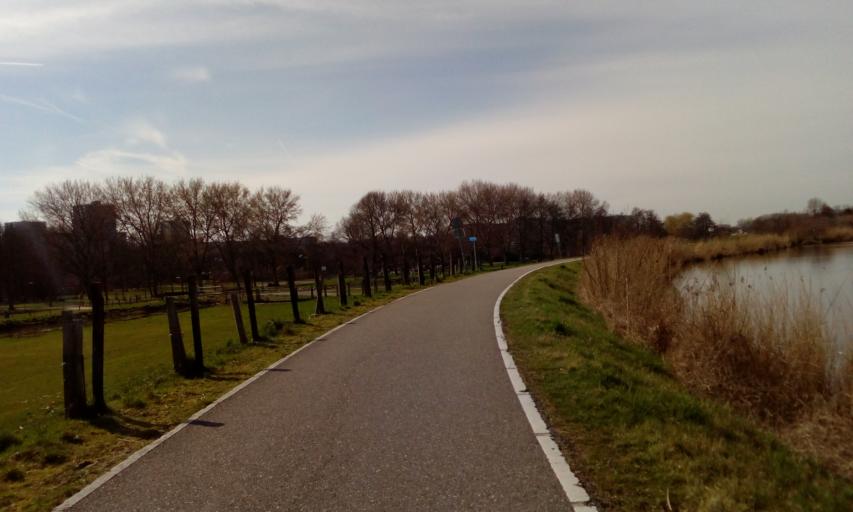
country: NL
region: South Holland
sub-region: Gemeente Lansingerland
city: Bleiswijk
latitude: 51.9683
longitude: 4.5355
